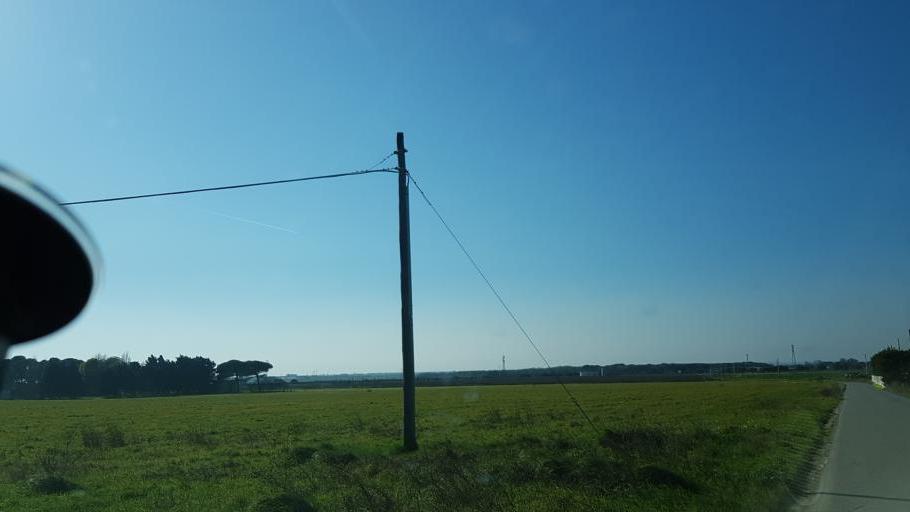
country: IT
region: Apulia
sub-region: Provincia di Brindisi
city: Brindisi
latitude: 40.6576
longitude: 17.9031
